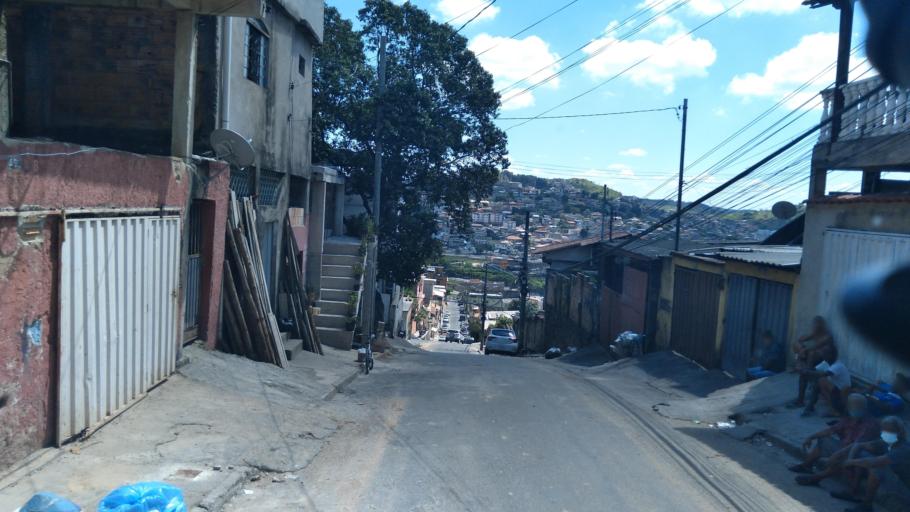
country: BR
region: Minas Gerais
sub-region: Belo Horizonte
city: Belo Horizonte
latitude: -19.9084
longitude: -43.8887
